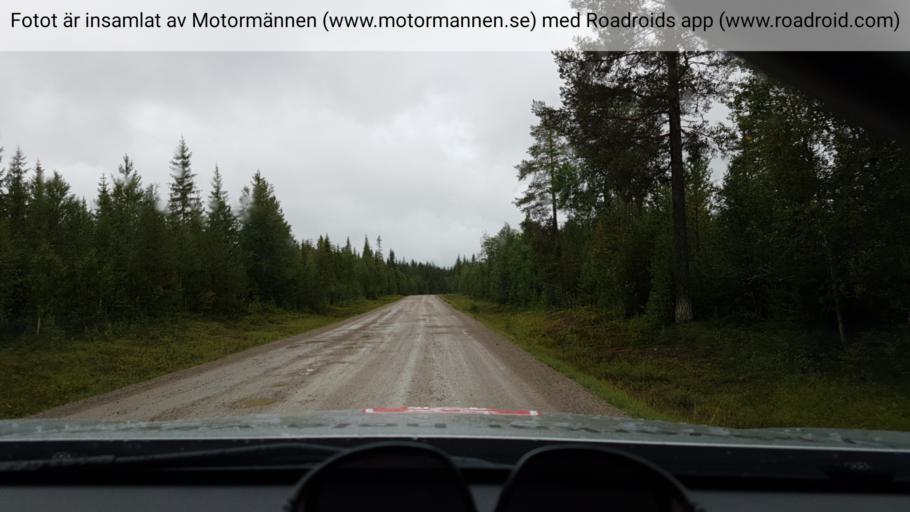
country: SE
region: Vaesterbotten
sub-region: Lycksele Kommun
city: Soderfors
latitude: 64.7575
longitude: 17.6576
